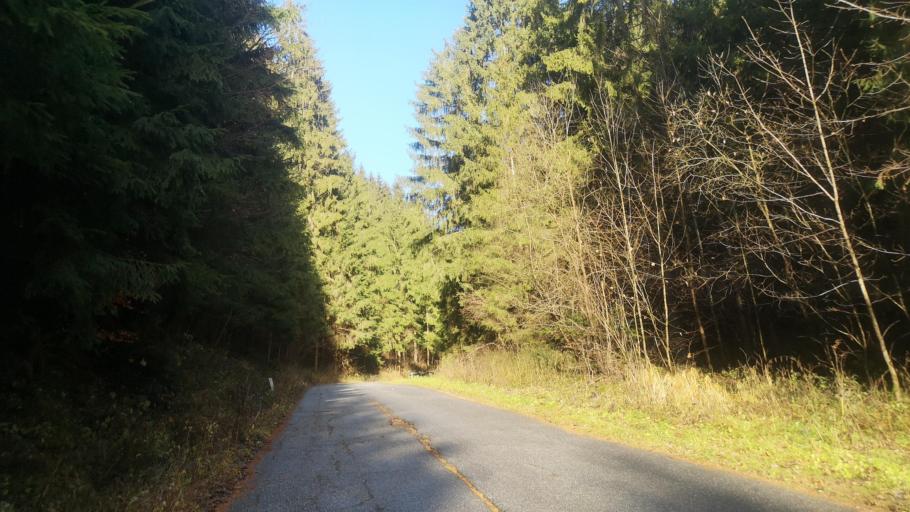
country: SK
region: Banskobystricky
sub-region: Okres Ziar nad Hronom
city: Kremnica
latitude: 48.7611
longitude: 18.9271
